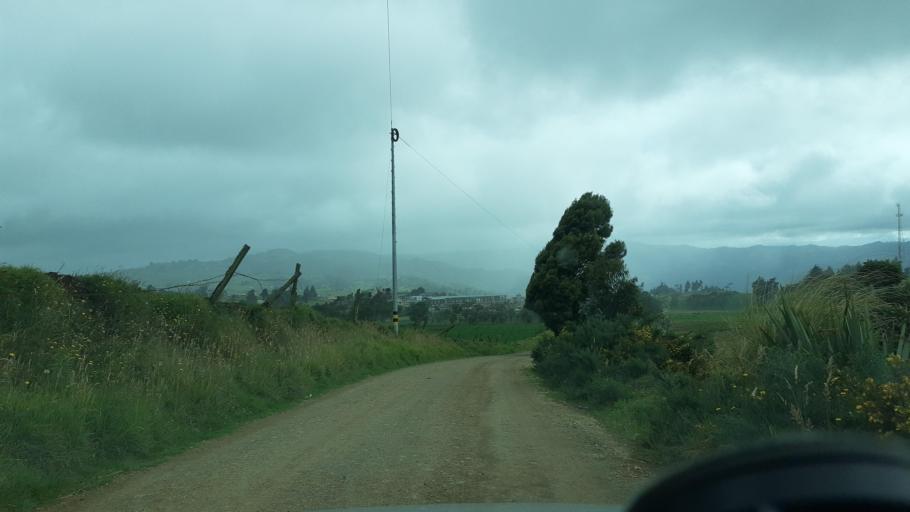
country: CO
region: Boyaca
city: Samaca
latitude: 5.4894
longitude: -73.4604
